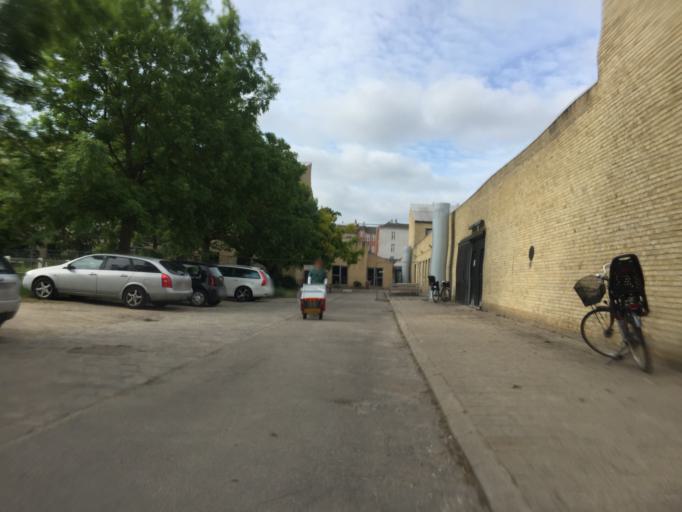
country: DK
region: Capital Region
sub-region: Frederiksberg Kommune
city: Frederiksberg
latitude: 55.6802
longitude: 12.5394
